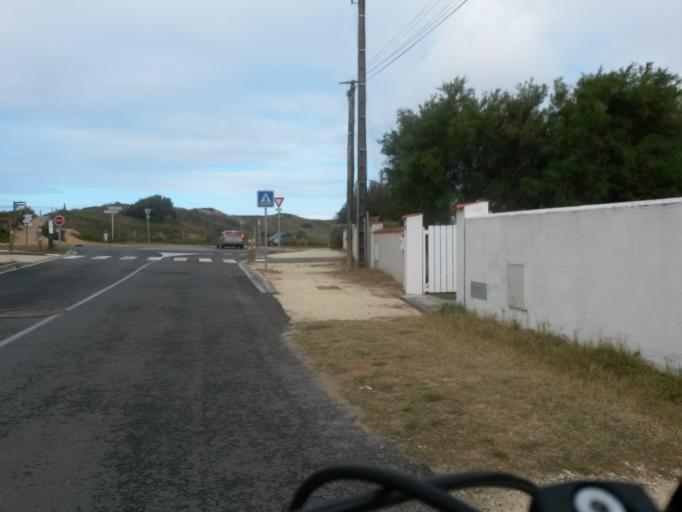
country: FR
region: Poitou-Charentes
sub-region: Departement de la Charente-Maritime
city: Saint-Denis-d'Oleron
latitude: 45.9396
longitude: -1.3666
